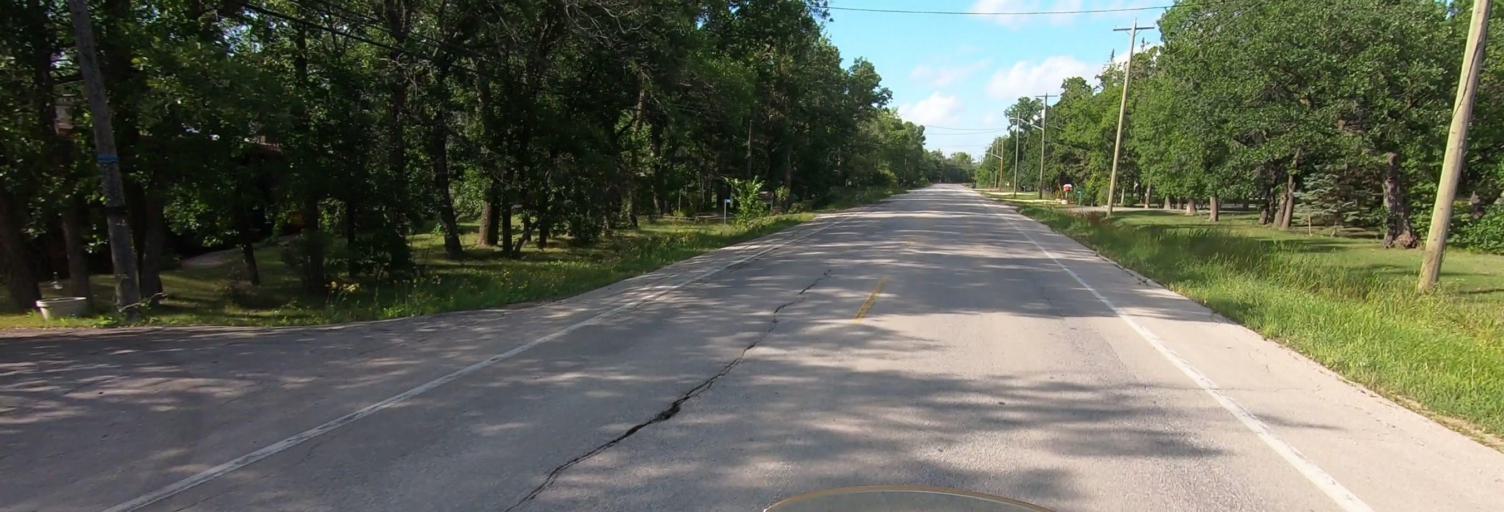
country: CA
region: Manitoba
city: Winnipeg
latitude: 50.0042
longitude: -97.0379
